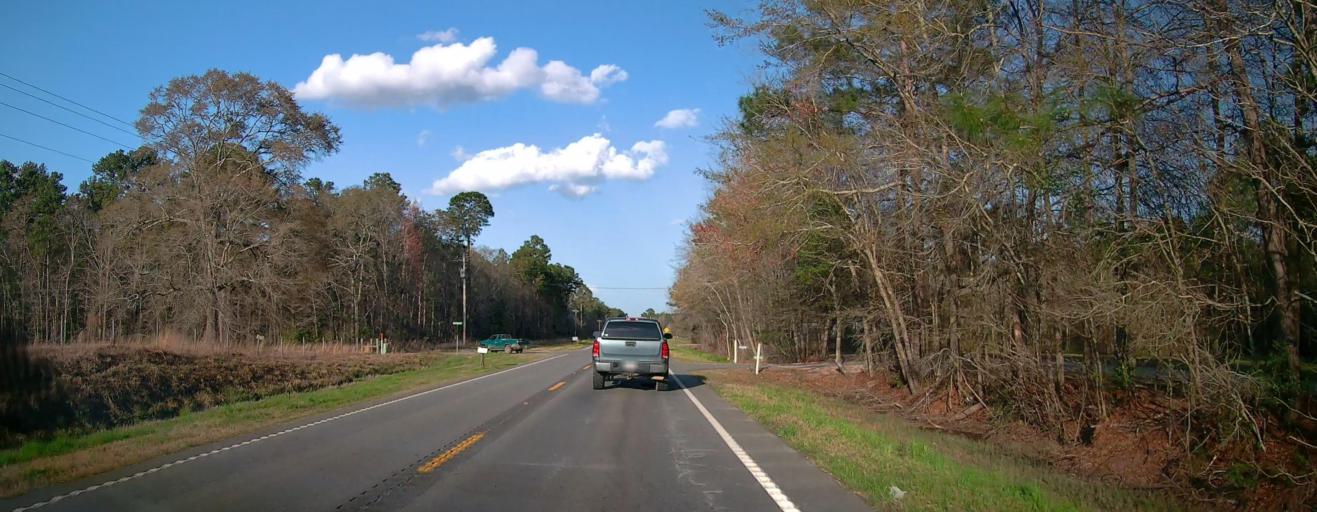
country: US
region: Georgia
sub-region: Tattnall County
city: Reidsville
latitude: 32.1281
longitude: -82.0548
